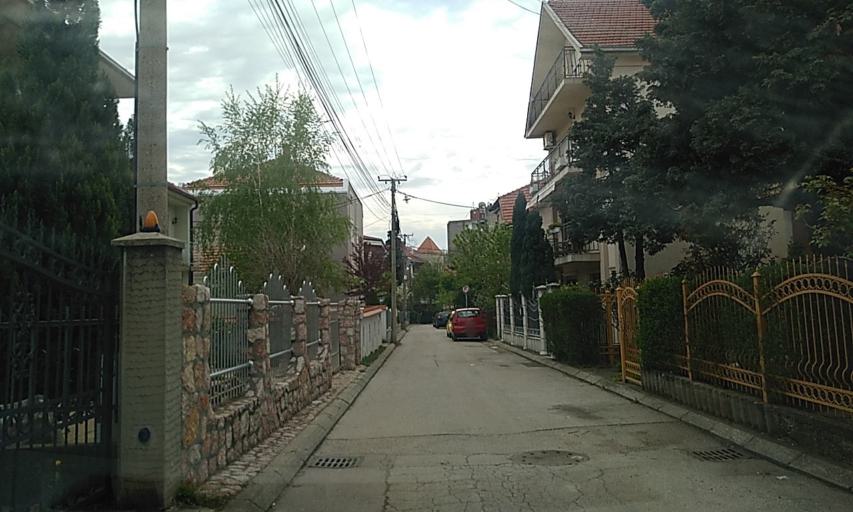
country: RS
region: Central Serbia
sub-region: Nisavski Okrug
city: Nis
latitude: 43.3357
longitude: 21.9156
